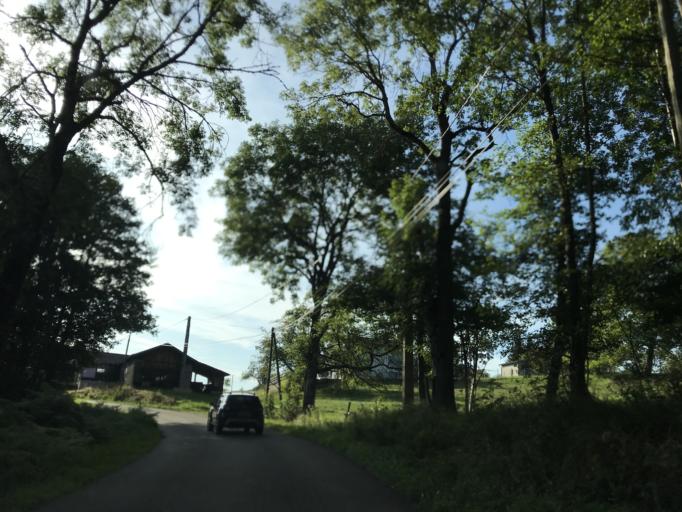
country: FR
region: Auvergne
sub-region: Departement du Puy-de-Dome
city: Job
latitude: 45.7100
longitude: 3.7191
